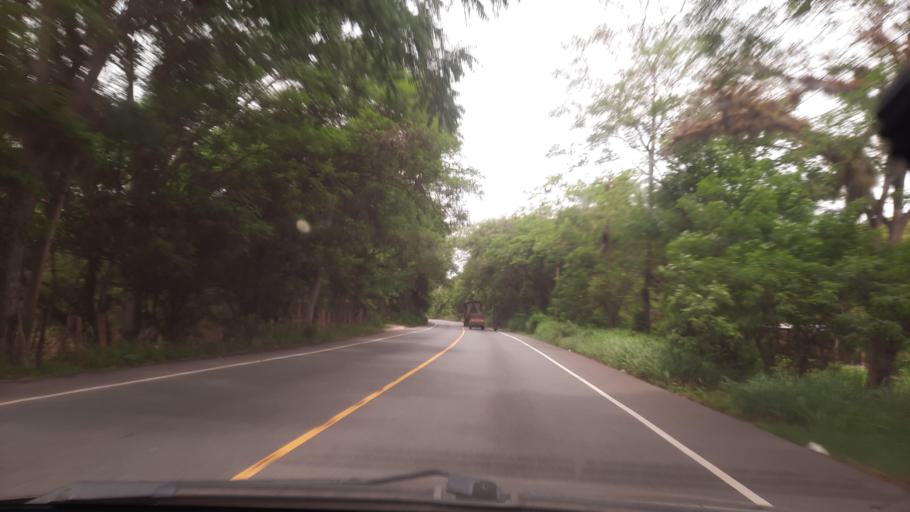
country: GT
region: Izabal
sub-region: Municipio de Los Amates
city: Los Amates
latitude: 15.2190
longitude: -89.2244
